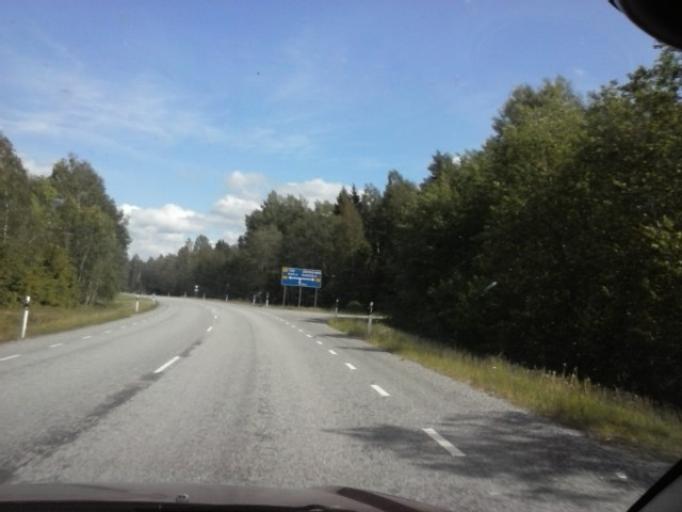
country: EE
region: Raplamaa
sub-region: Rapla vald
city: Rapla
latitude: 58.9903
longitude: 24.7790
